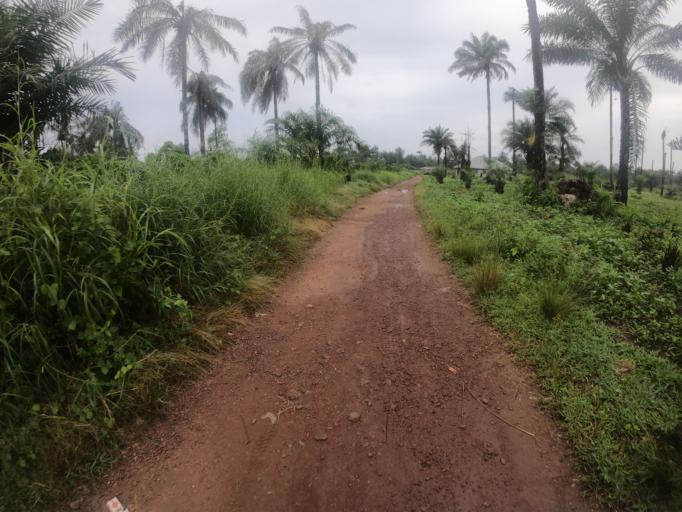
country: SL
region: Northern Province
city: Port Loko
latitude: 8.4981
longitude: -12.7511
